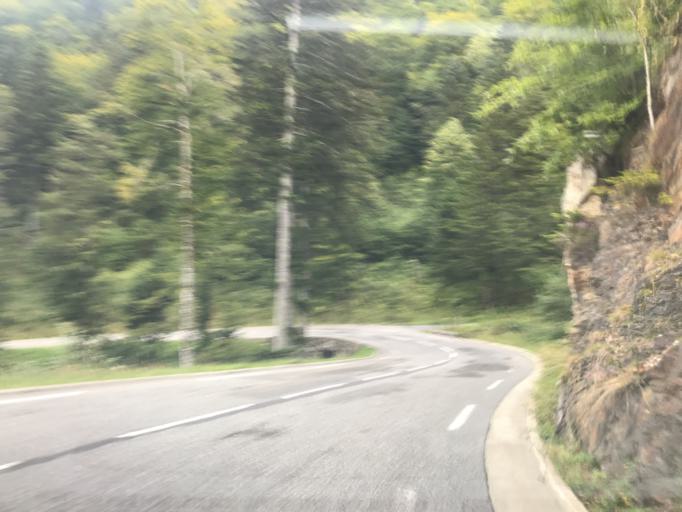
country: ES
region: Catalonia
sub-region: Provincia de Lleida
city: Les
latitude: 42.7720
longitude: 0.6615
